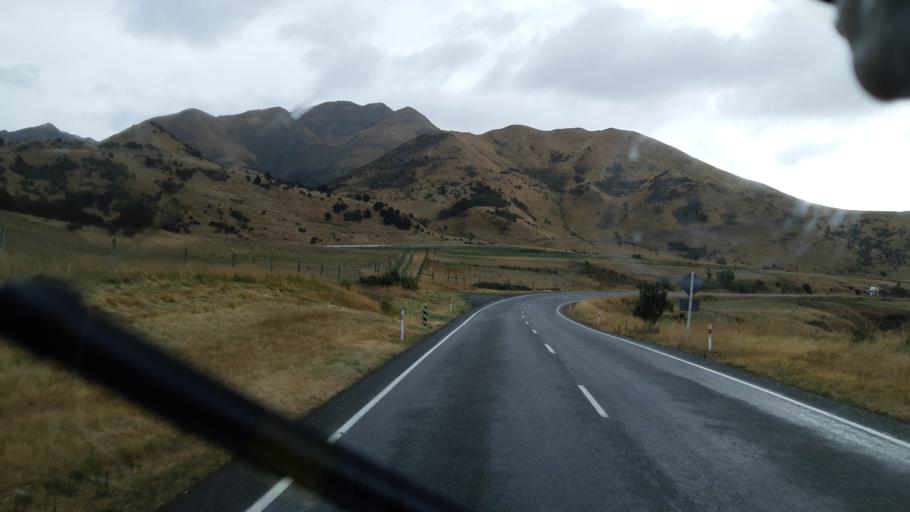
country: NZ
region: Canterbury
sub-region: Hurunui District
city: Amberley
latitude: -42.6419
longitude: 172.7723
